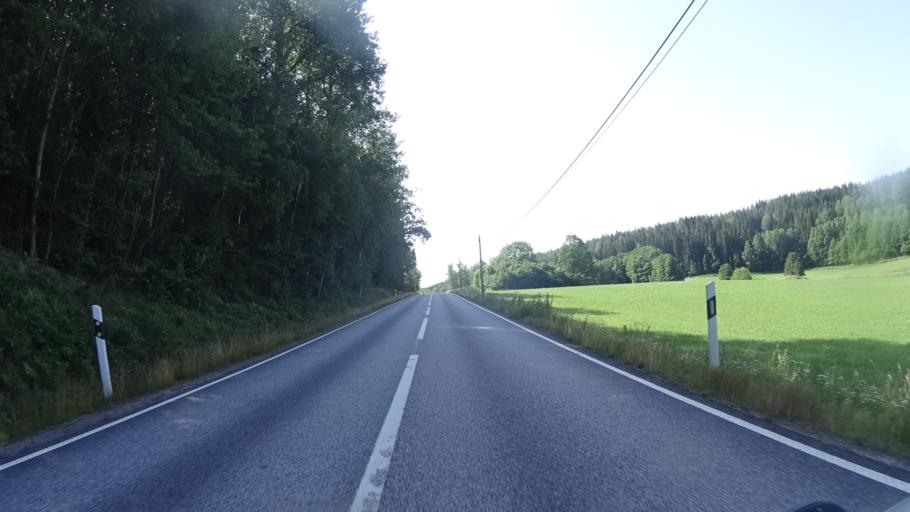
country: SE
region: Kalmar
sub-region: Vasterviks Kommun
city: Overum
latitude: 58.0120
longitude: 16.2624
